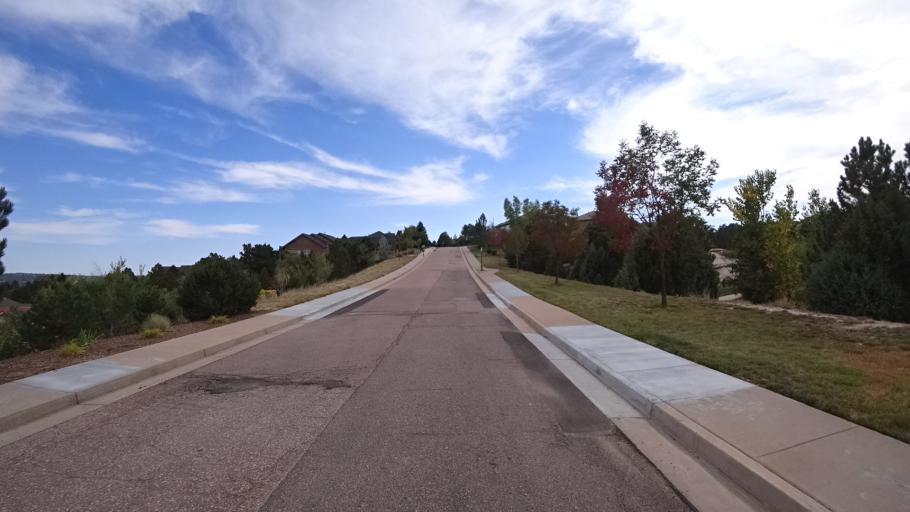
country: US
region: Colorado
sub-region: El Paso County
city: Colorado Springs
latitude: 38.9018
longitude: -104.7906
